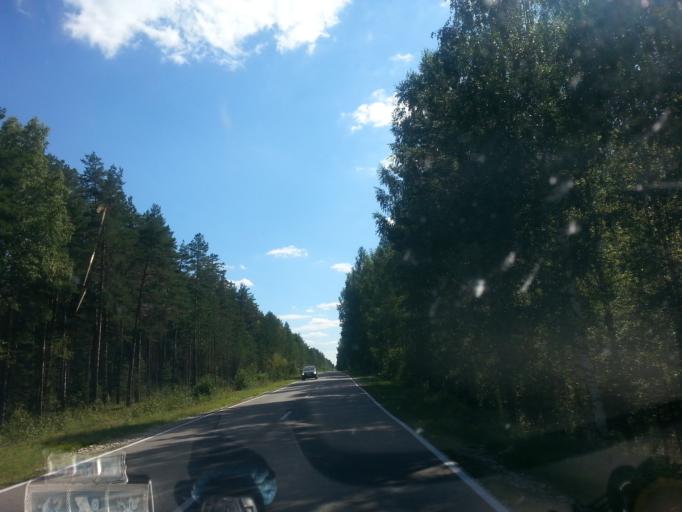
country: RU
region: Vladimir
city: Galitsy
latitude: 56.1185
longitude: 42.8724
